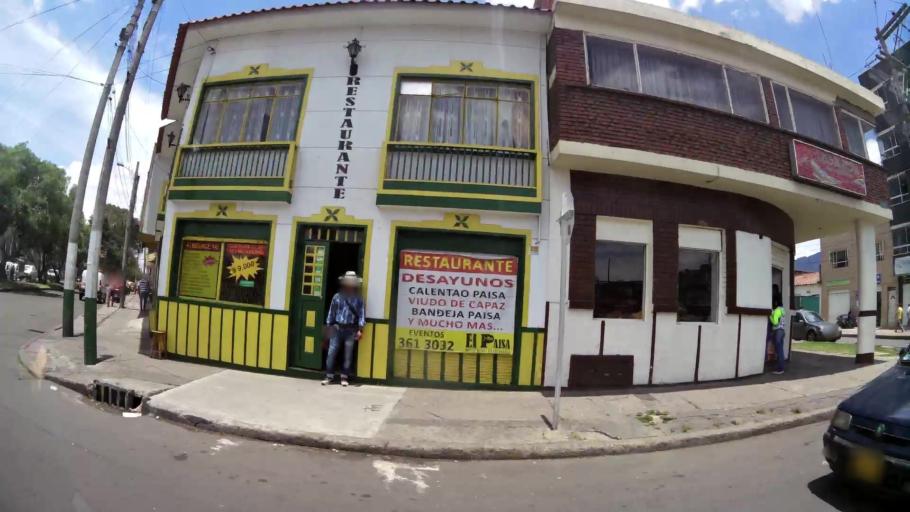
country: CO
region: Bogota D.C.
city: Bogota
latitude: 4.5900
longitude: -74.1043
